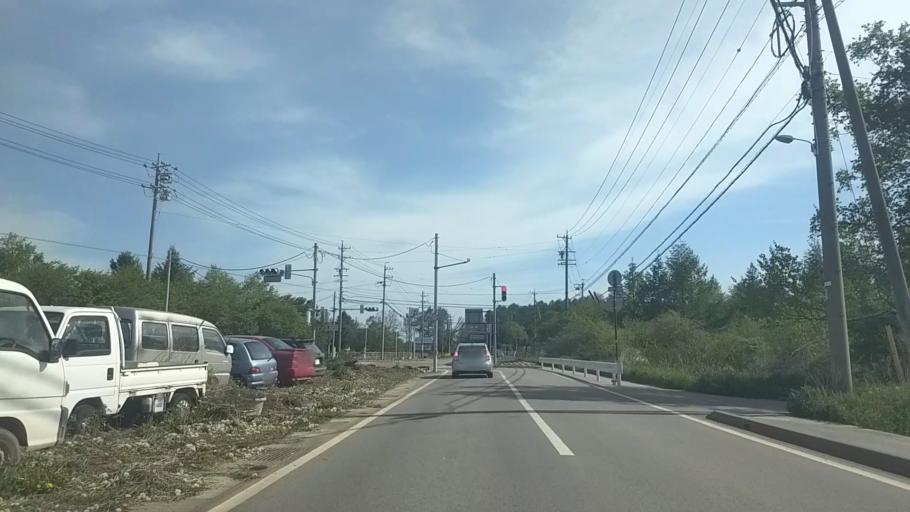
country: JP
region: Nagano
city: Saku
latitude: 35.9581
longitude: 138.4747
